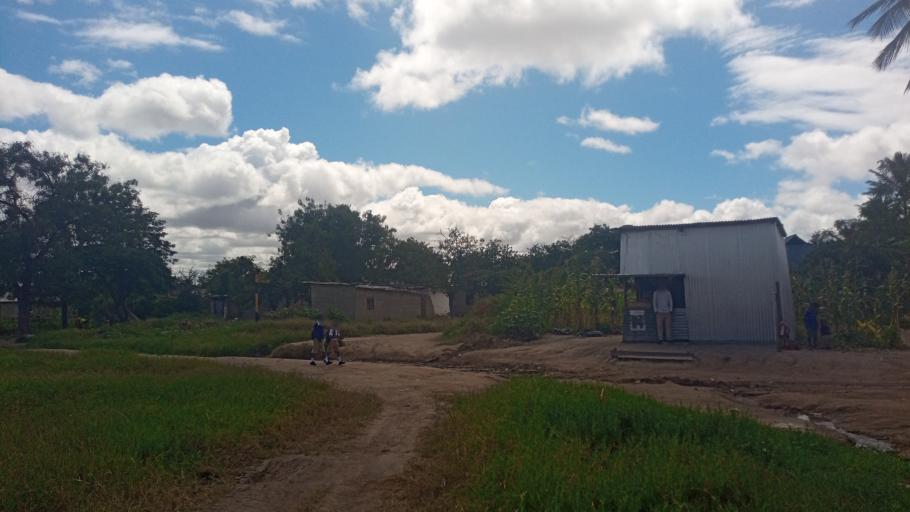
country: TZ
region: Dodoma
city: Dodoma
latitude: -6.1908
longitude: 35.7273
